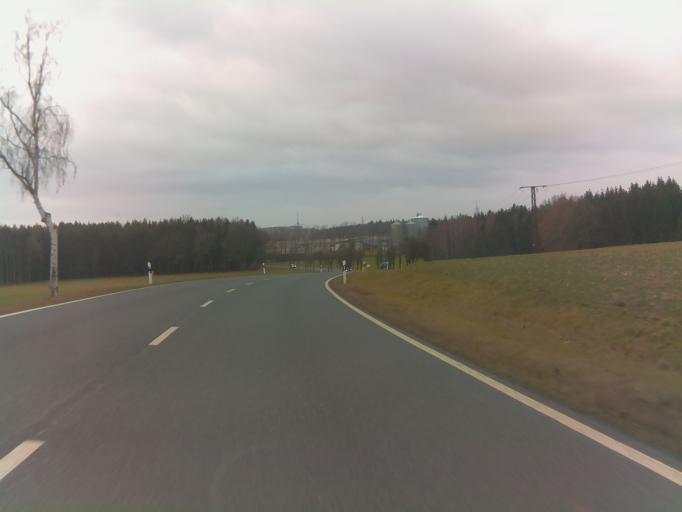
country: DE
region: Thuringia
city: Langenwolschendorf
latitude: 50.6734
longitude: 11.9402
